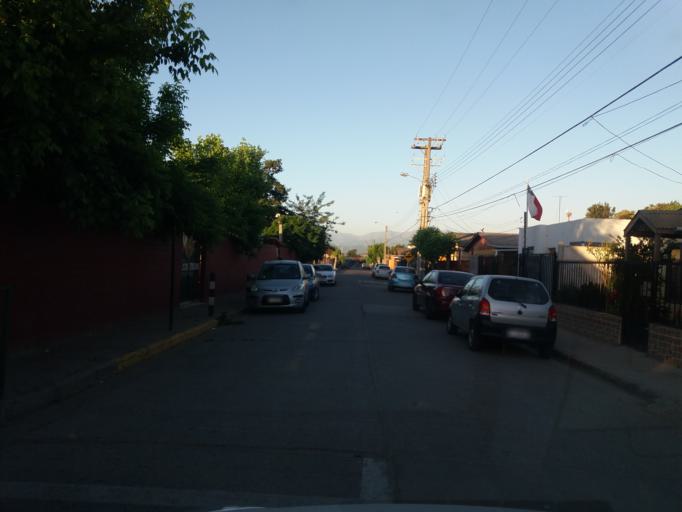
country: CL
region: Valparaiso
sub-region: Provincia de Quillota
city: Quillota
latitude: -32.9372
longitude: -71.2770
